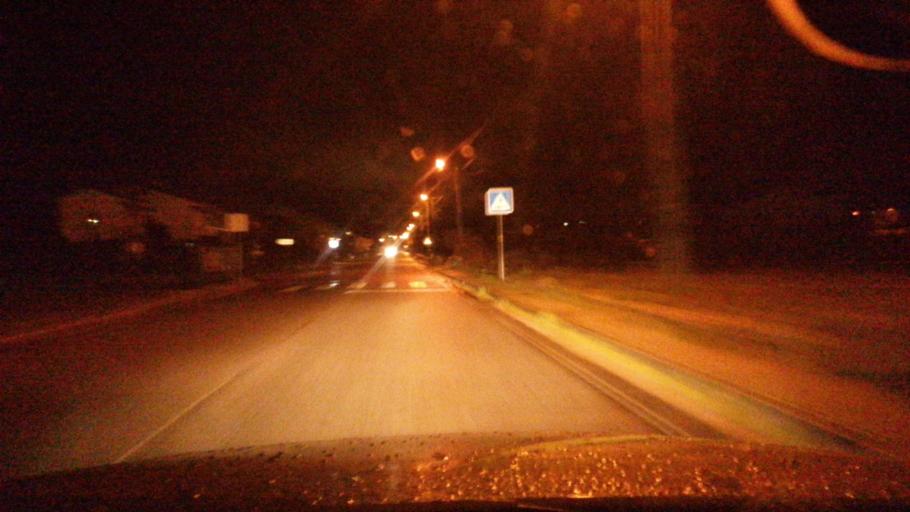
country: PT
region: Viseu
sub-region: Moimenta da Beira
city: Moimenta da Beira
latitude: 40.9389
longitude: -7.5652
